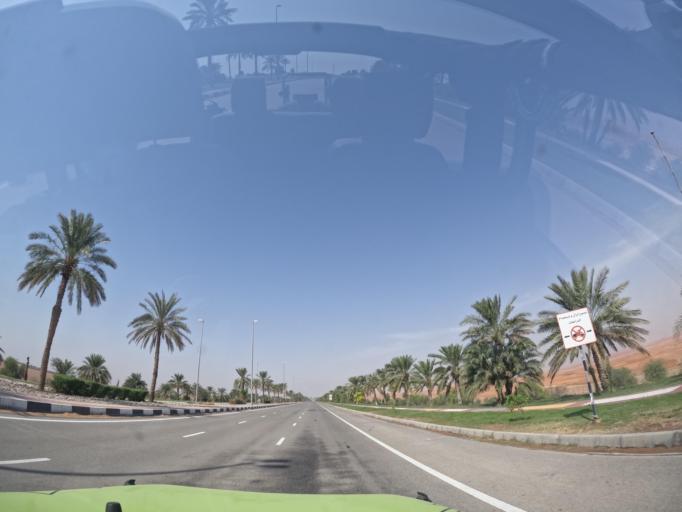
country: AE
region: Abu Dhabi
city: Al Ain
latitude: 24.2627
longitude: 55.6671
